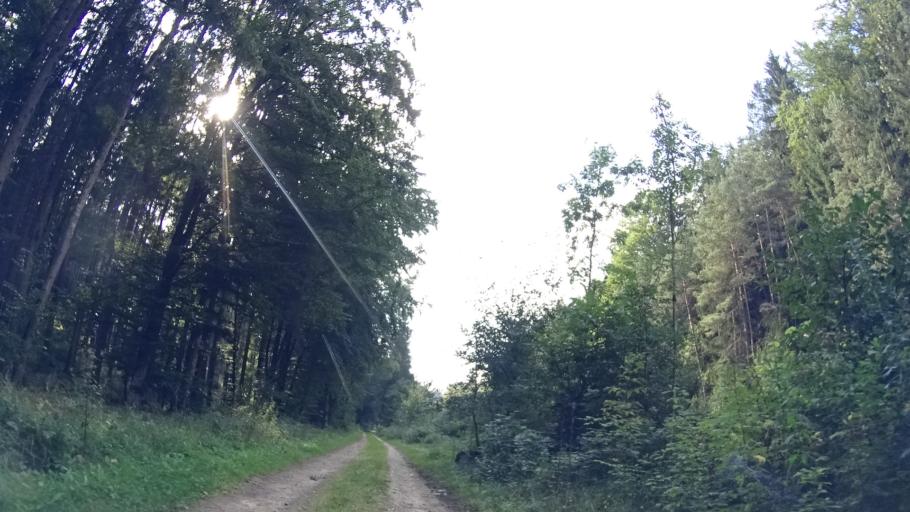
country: DE
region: Bavaria
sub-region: Lower Bavaria
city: Riedenburg
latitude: 48.9444
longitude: 11.6776
